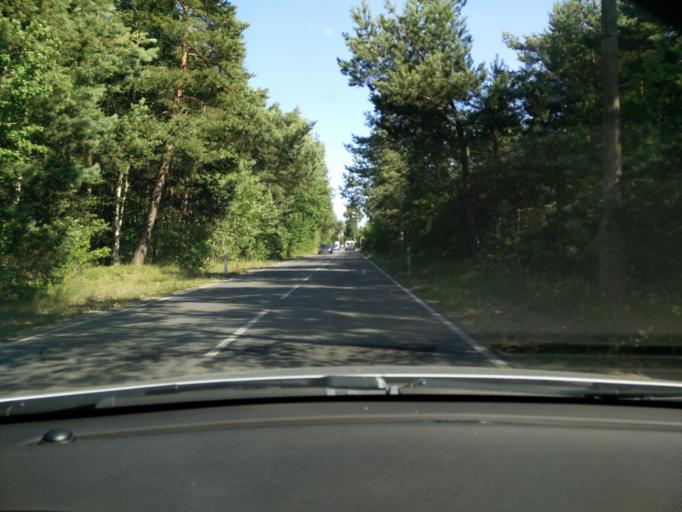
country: PL
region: Pomeranian Voivodeship
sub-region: Powiat pucki
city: Jastarnia
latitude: 54.7145
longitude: 18.6363
